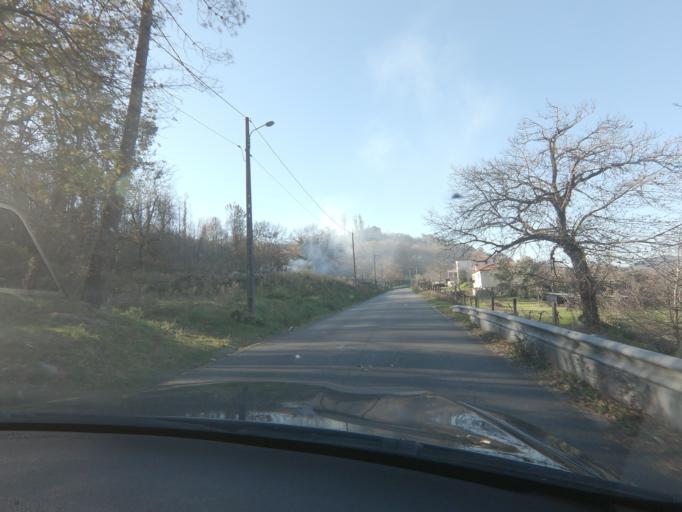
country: PT
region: Viseu
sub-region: Oliveira de Frades
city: Oliveira de Frades
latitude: 40.7287
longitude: -8.1514
